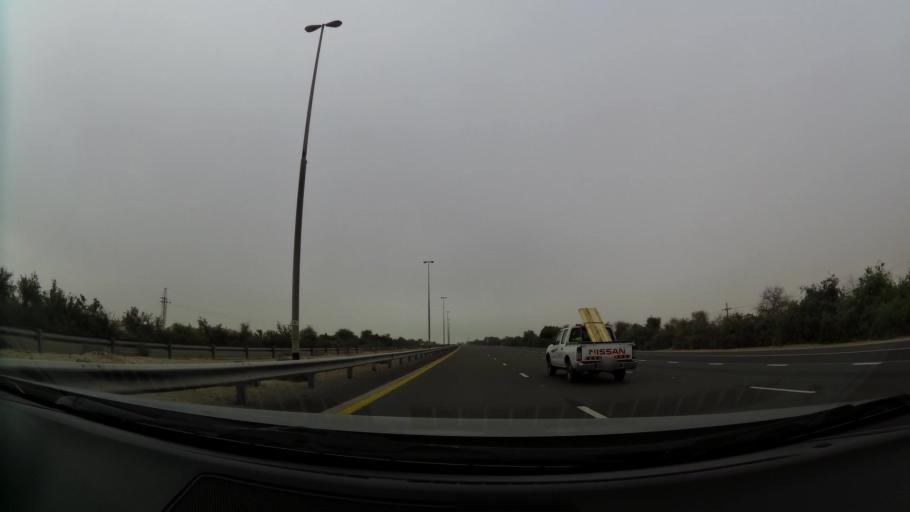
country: AE
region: Dubai
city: Dubai
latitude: 25.0583
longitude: 55.4177
